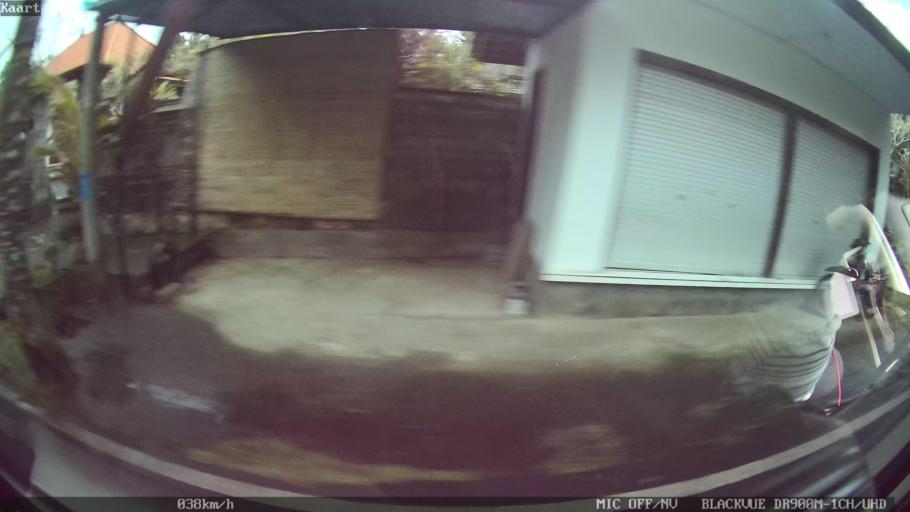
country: ID
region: Bali
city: Pegongan
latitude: -8.4932
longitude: 115.2370
